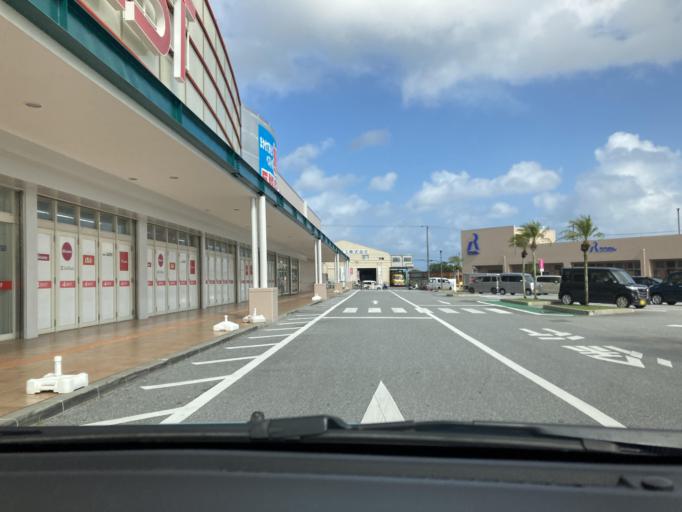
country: JP
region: Okinawa
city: Ginowan
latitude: 26.2529
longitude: 127.7363
